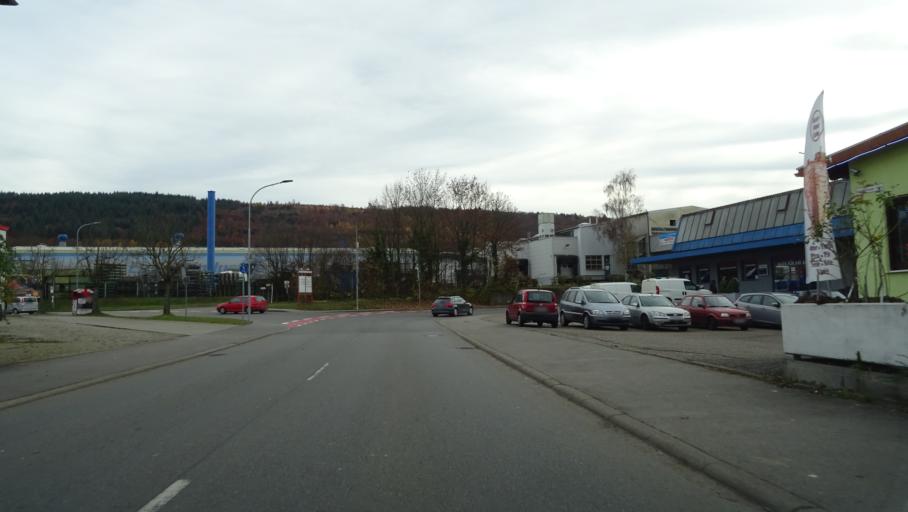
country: DE
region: Baden-Wuerttemberg
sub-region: Karlsruhe Region
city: Neckarzimmern
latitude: 49.3449
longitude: 9.1252
